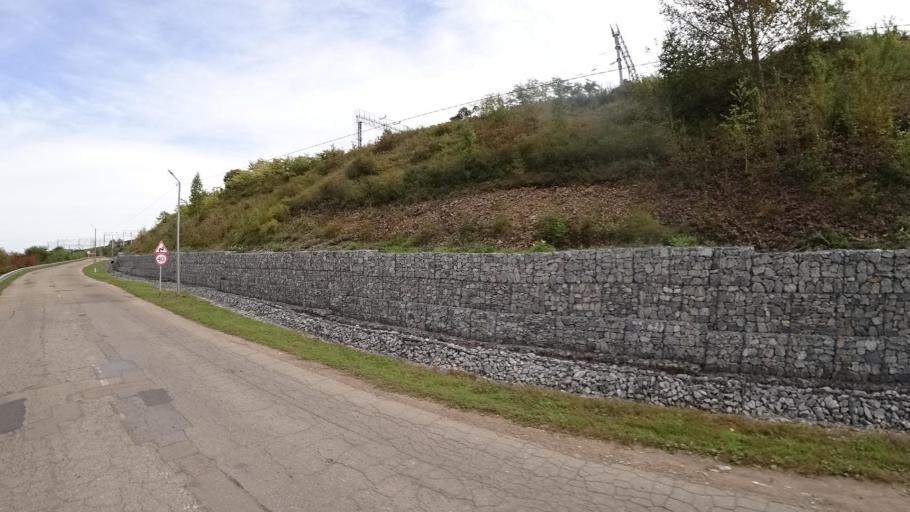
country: RU
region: Jewish Autonomous Oblast
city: Khingansk
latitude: 48.9979
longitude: 131.0572
